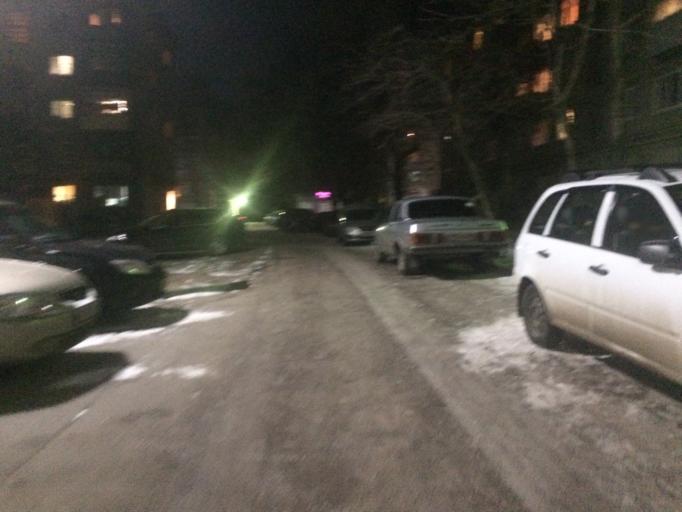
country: RU
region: Rjazan
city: Ryazan'
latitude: 54.6221
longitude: 39.7223
